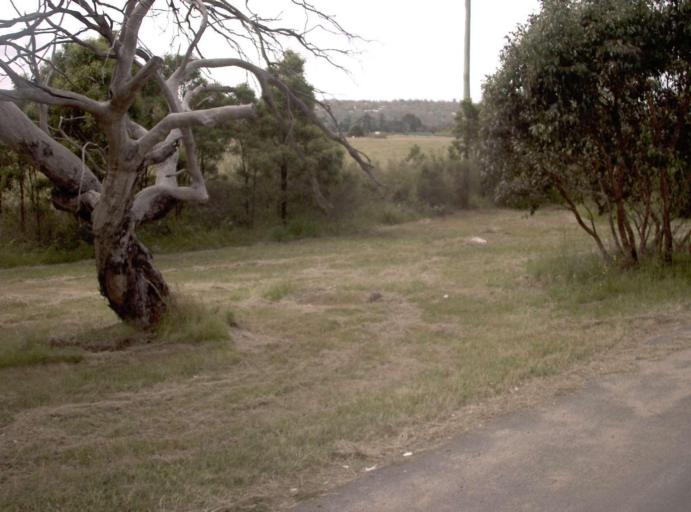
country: AU
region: Victoria
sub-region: Mornington Peninsula
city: Moorooduc
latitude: -38.2292
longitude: 145.0943
